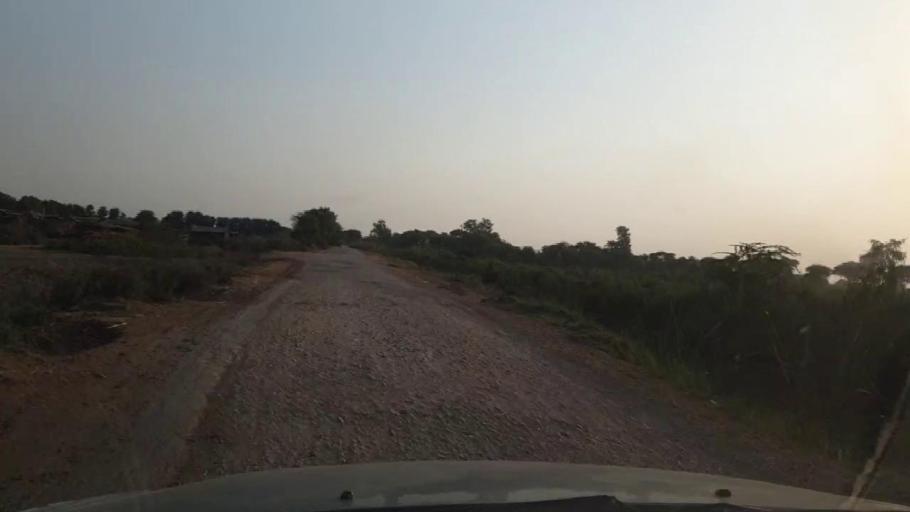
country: PK
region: Sindh
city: Tando Muhammad Khan
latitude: 25.0192
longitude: 68.4390
